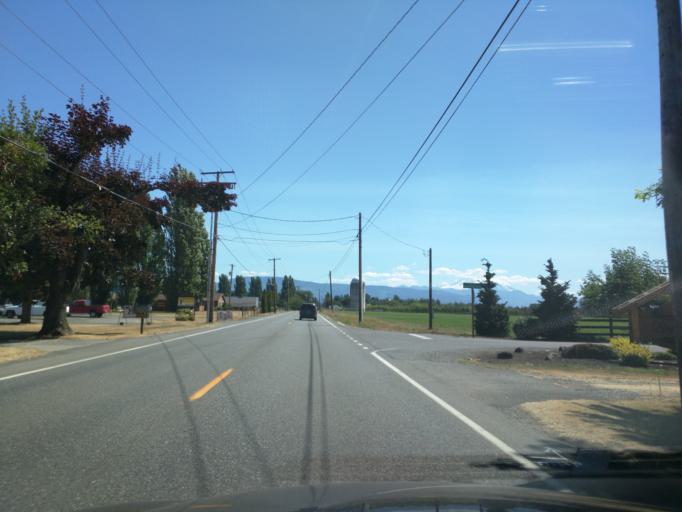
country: US
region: Washington
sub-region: Whatcom County
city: Lynden
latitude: 48.8916
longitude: -122.4784
